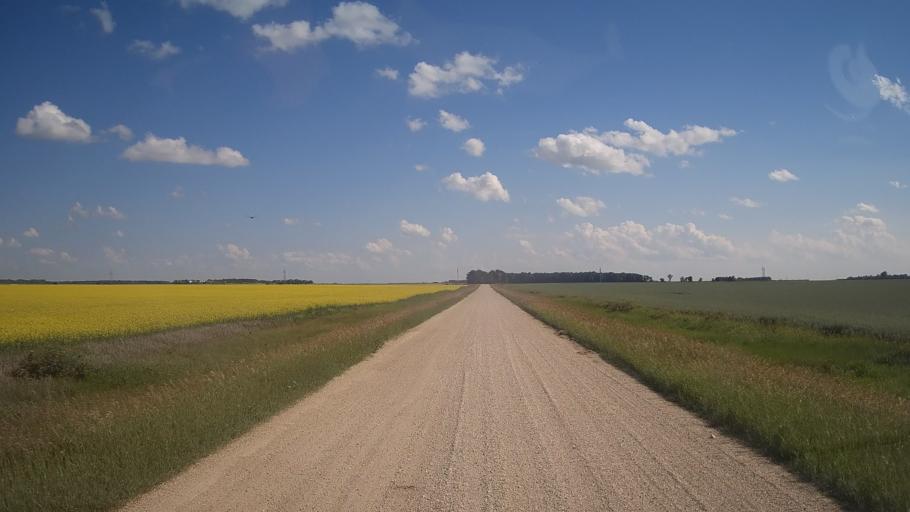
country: CA
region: Manitoba
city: Stonewall
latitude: 50.1292
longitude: -97.5054
